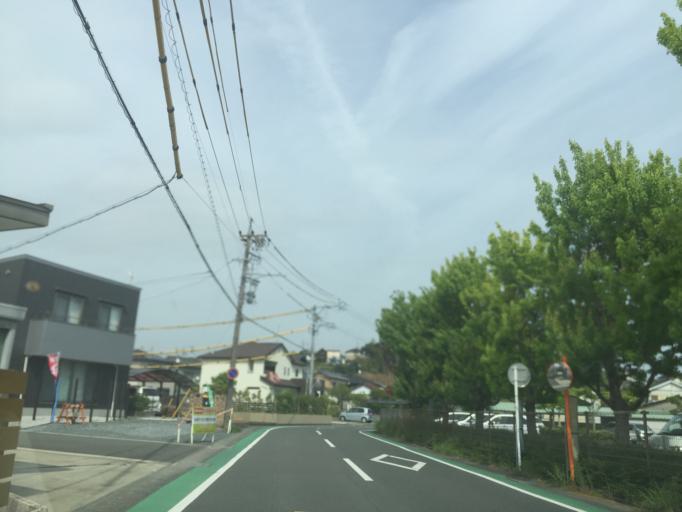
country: JP
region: Shizuoka
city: Kakegawa
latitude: 34.7820
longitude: 138.0184
